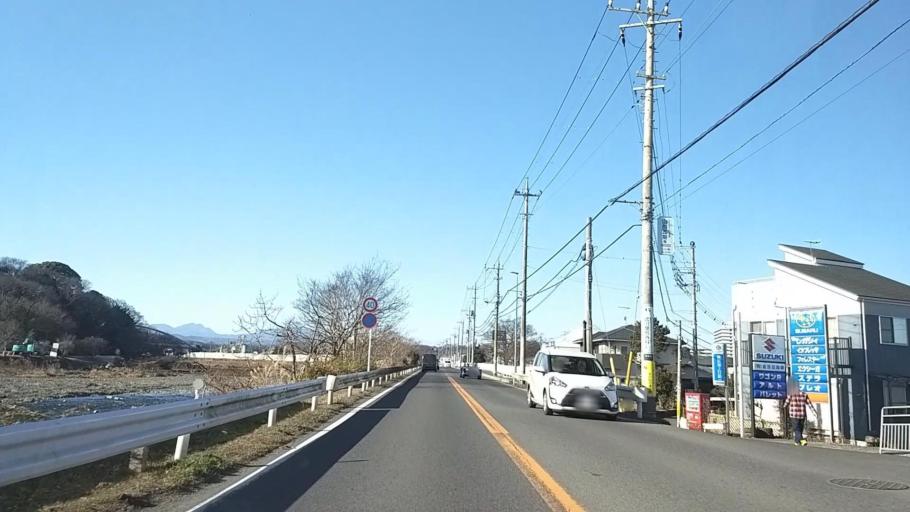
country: JP
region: Kanagawa
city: Isehara
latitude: 35.3598
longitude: 139.2852
